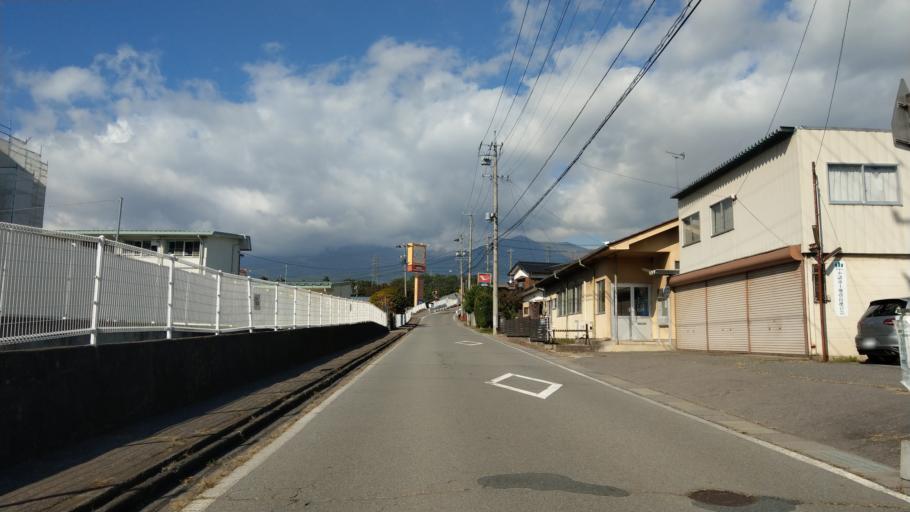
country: JP
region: Nagano
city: Komoro
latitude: 36.3169
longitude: 138.4409
